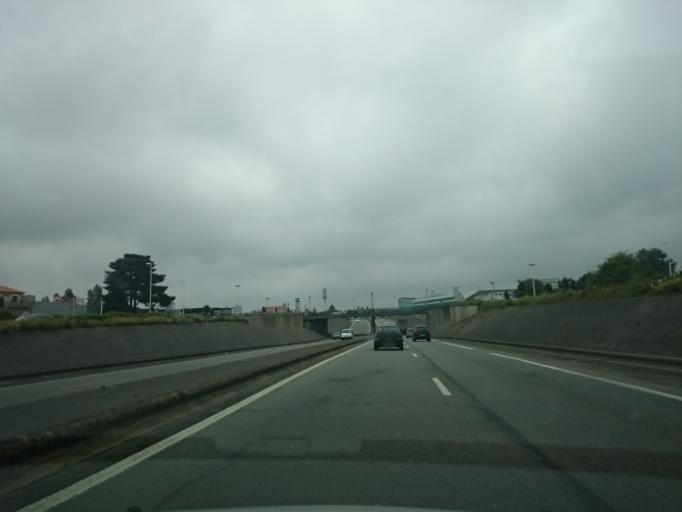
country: FR
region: Pays de la Loire
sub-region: Departement de la Loire-Atlantique
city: Saint-Herblain
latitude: 47.2287
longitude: -1.6371
